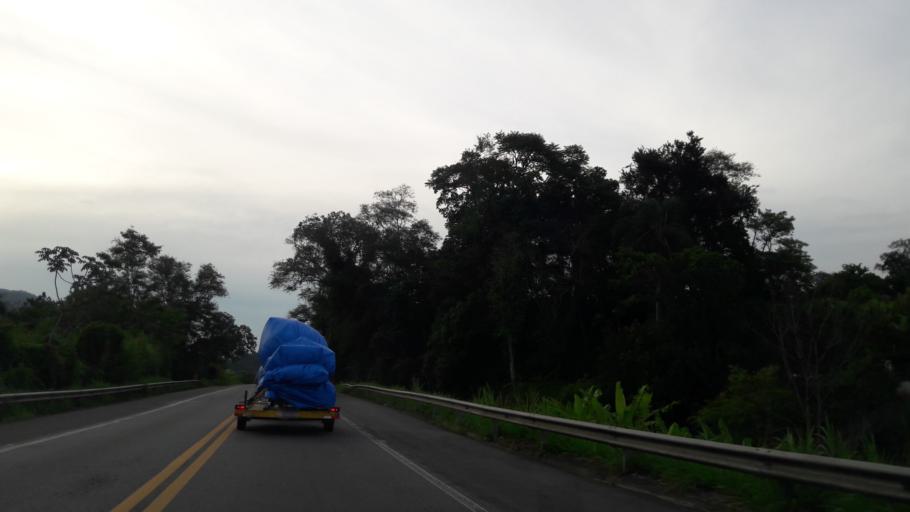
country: BR
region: Sao Paulo
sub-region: Miracatu
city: Miracatu
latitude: -24.2767
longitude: -47.2471
